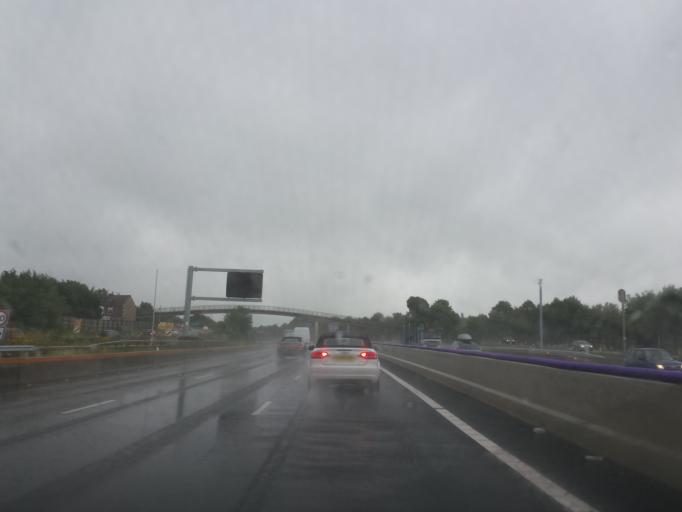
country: GB
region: England
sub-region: Derbyshire
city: Blackwell
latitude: 53.1055
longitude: -1.3272
